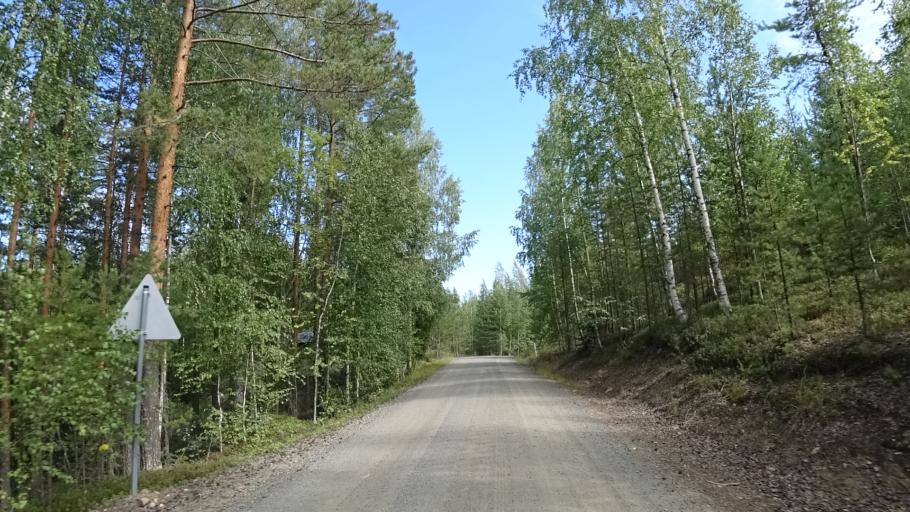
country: FI
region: North Karelia
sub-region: Joensuu
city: Pyhaeselkae
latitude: 62.3733
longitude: 29.8246
